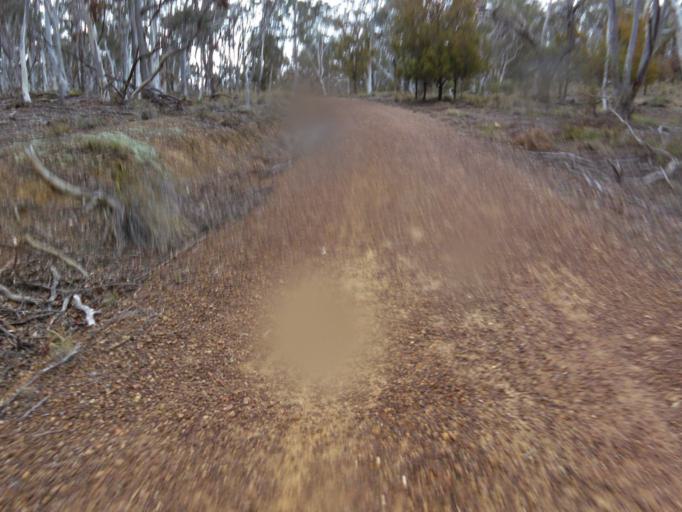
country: AU
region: Australian Capital Territory
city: Acton
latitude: -35.2640
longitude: 149.0971
